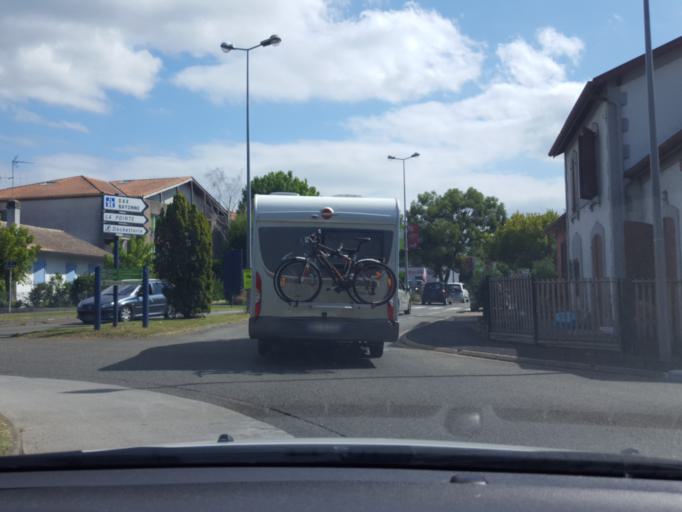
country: FR
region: Aquitaine
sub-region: Departement des Landes
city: Capbreton
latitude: 43.6410
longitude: -1.4256
